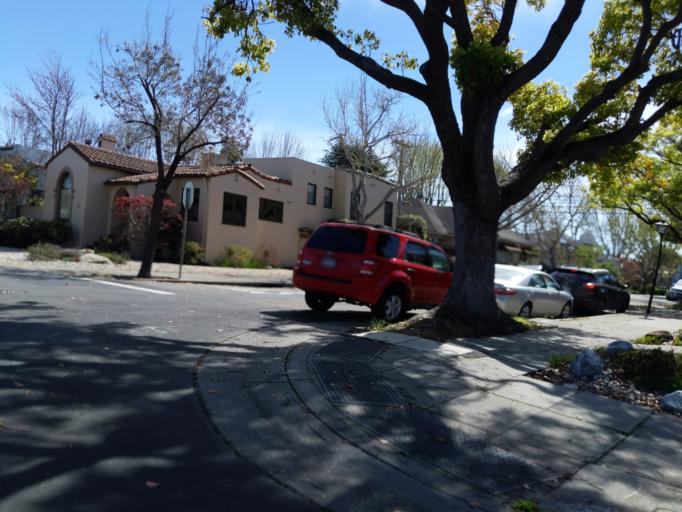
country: US
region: California
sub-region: Alameda County
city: Alameda
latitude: 37.7643
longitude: -122.2277
